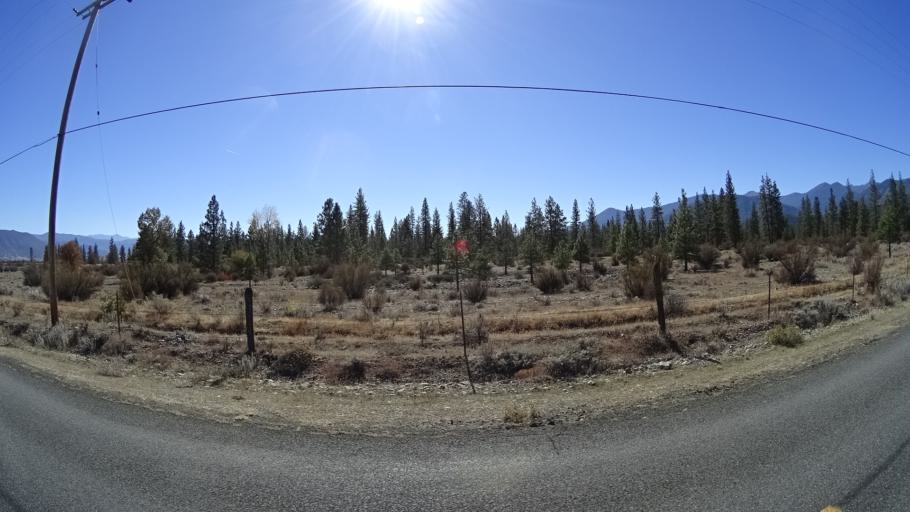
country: US
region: California
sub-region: Siskiyou County
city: Yreka
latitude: 41.5395
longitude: -122.9138
